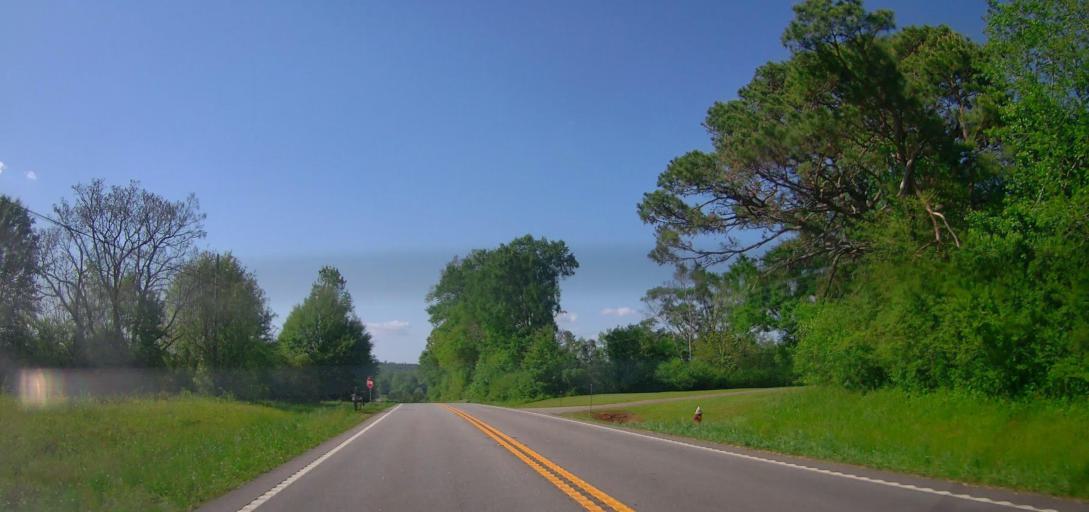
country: US
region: Georgia
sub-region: Morgan County
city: Madison
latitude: 33.6296
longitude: -83.4857
